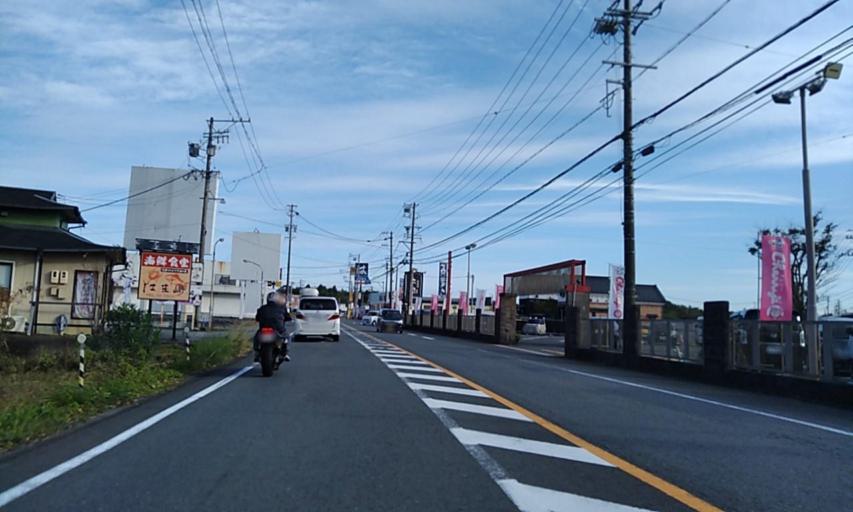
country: JP
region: Mie
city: Toba
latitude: 34.3456
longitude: 136.8134
